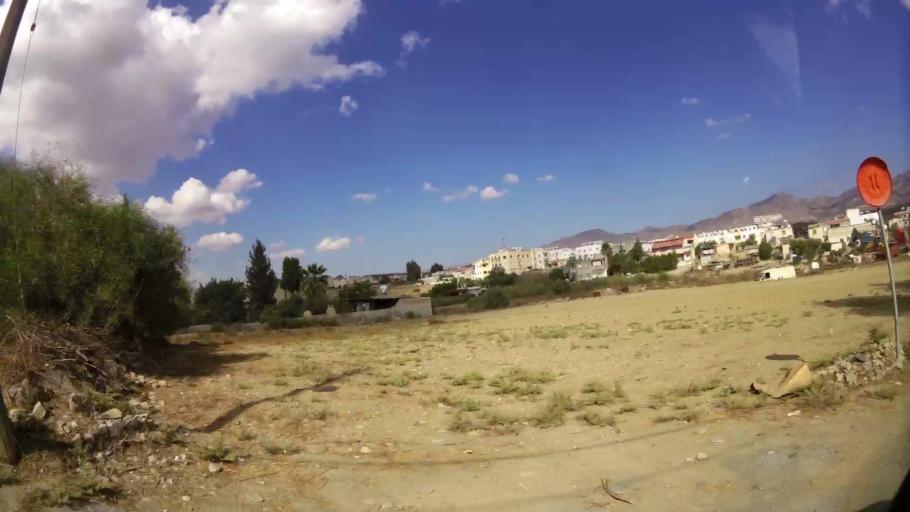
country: CY
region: Lefkosia
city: Nicosia
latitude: 35.2237
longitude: 33.3807
